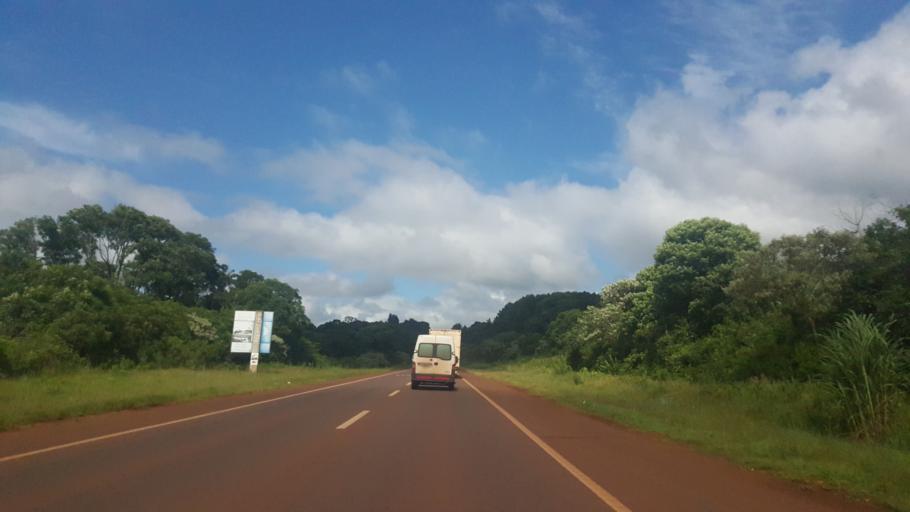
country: AR
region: Misiones
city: Aristobulo del Valle
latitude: -27.0855
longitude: -54.8421
